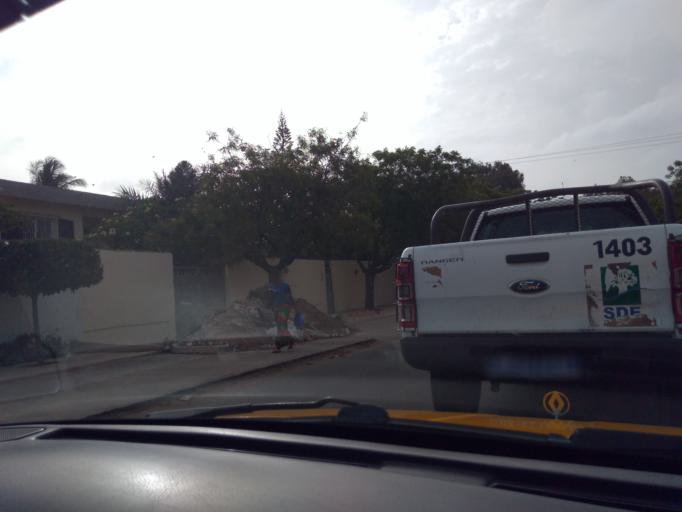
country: SN
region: Dakar
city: Grand Dakar
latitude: 14.7278
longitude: -17.4372
